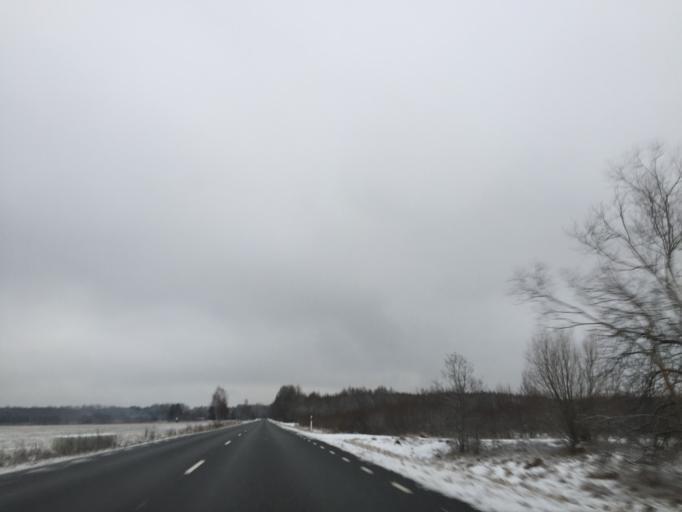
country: EE
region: Laeaene
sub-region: Lihula vald
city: Lihula
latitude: 58.6605
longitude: 23.8361
